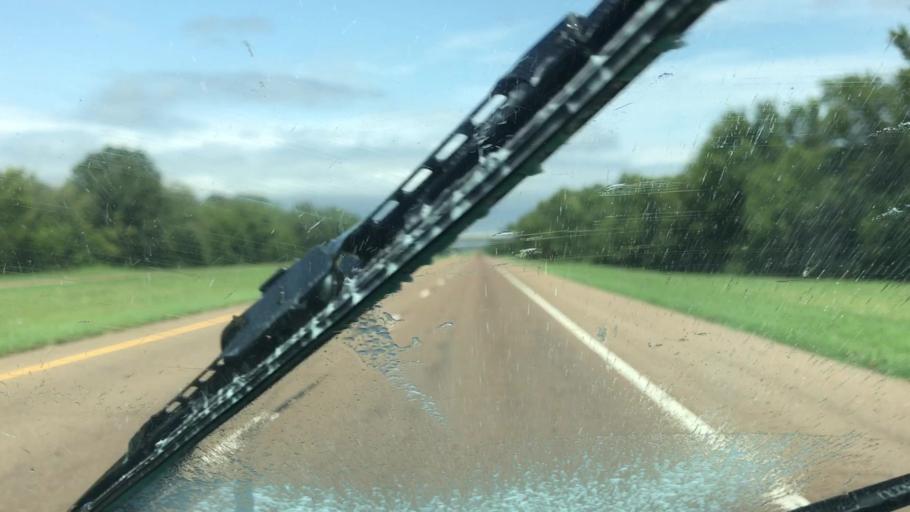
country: US
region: Tennessee
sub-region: Obion County
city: South Fulton
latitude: 36.4809
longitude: -88.9439
